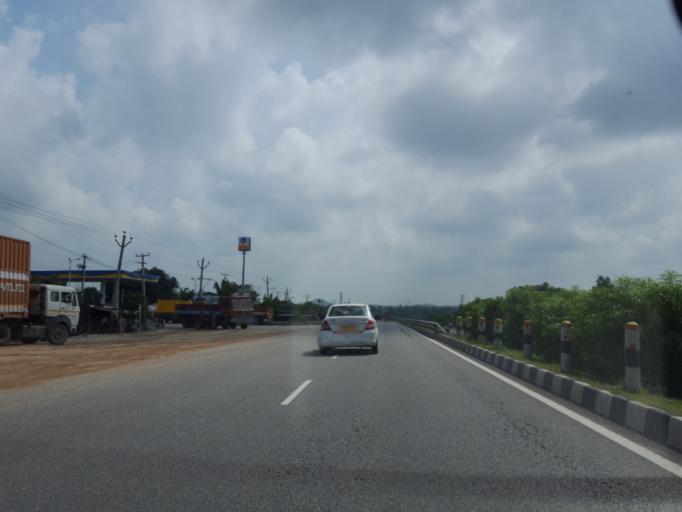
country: IN
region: Telangana
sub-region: Nalgonda
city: Bhongir
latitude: 17.2295
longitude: 78.9991
